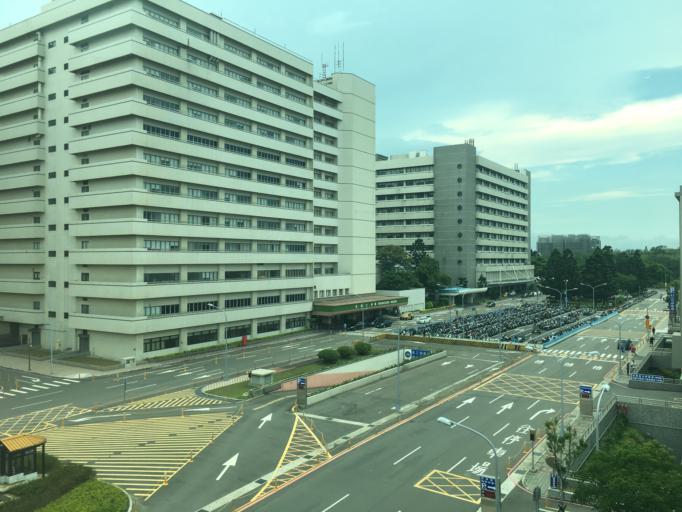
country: TW
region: Taiwan
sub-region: Taoyuan
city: Taoyuan
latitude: 25.0623
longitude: 121.3694
